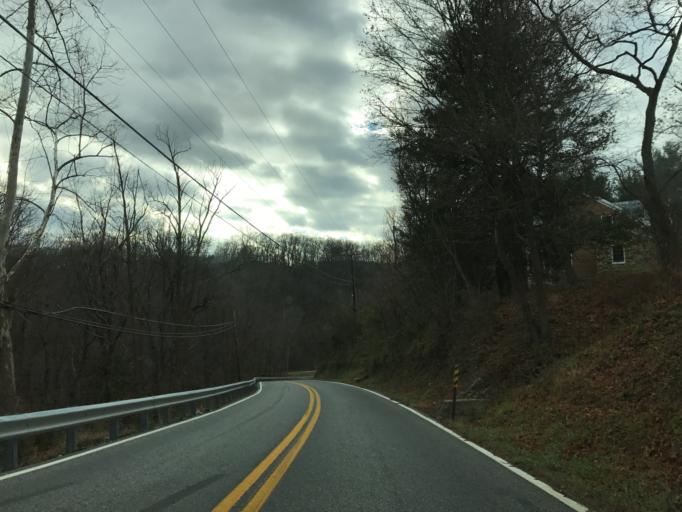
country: US
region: Pennsylvania
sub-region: York County
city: New Freedom
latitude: 39.6312
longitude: -76.6348
